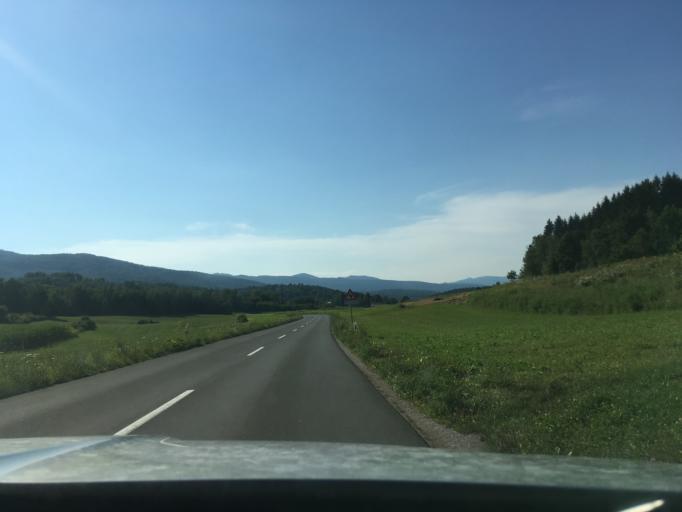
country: SI
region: Crnomelj
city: Crnomelj
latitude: 45.4838
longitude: 15.2002
